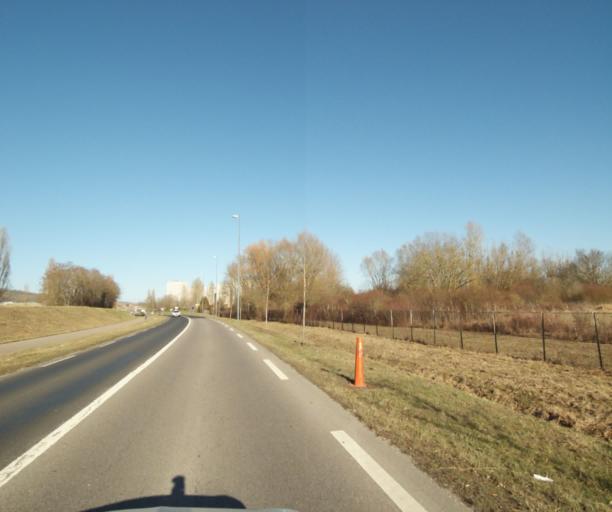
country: FR
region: Lorraine
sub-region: Departement de Meurthe-et-Moselle
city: Essey-les-Nancy
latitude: 48.6960
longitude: 6.2191
